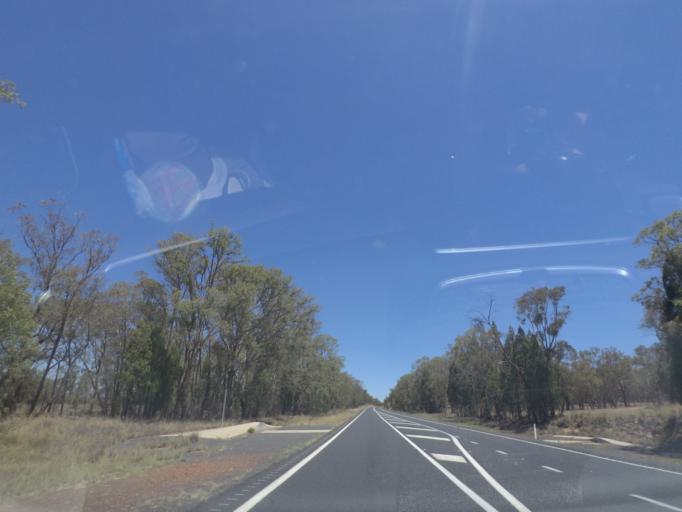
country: AU
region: New South Wales
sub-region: Warrumbungle Shire
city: Coonabarabran
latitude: -31.2260
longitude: 149.3222
